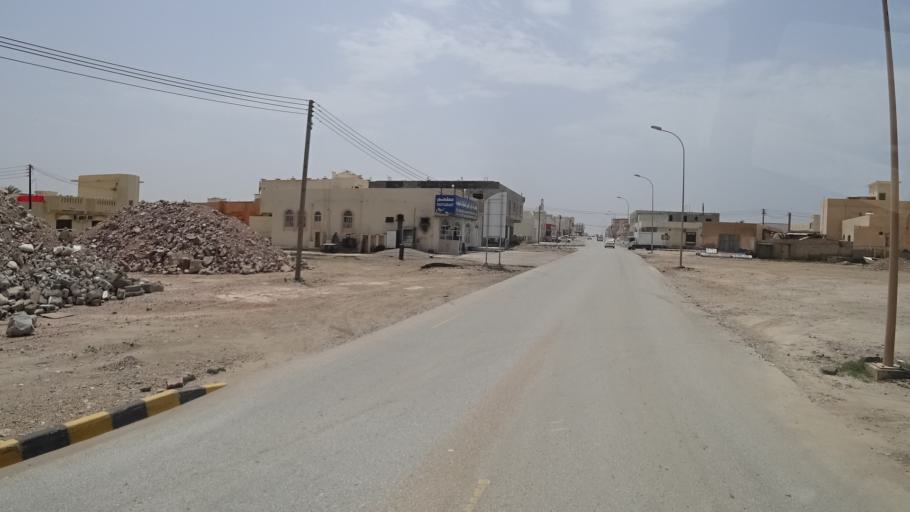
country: OM
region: Zufar
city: Salalah
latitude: 16.9832
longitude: 54.6890
